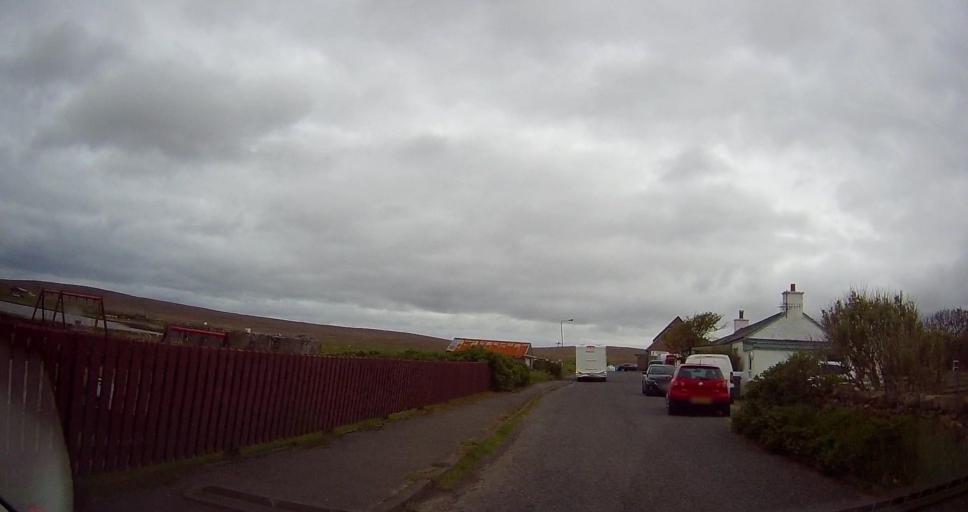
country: GB
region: Scotland
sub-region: Shetland Islands
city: Shetland
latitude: 60.7581
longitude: -0.8595
